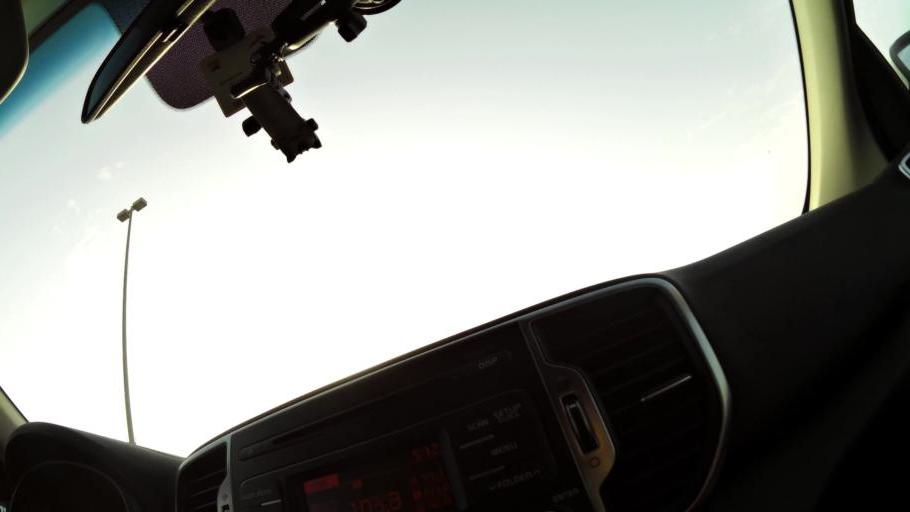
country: AE
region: Abu Dhabi
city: Abu Dhabi
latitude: 24.3370
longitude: 54.5051
